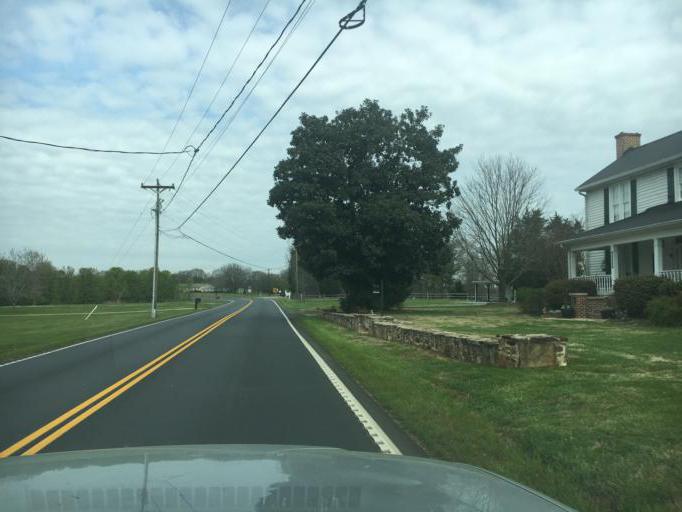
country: US
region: South Carolina
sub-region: Spartanburg County
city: Inman
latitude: 35.0225
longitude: -82.0840
